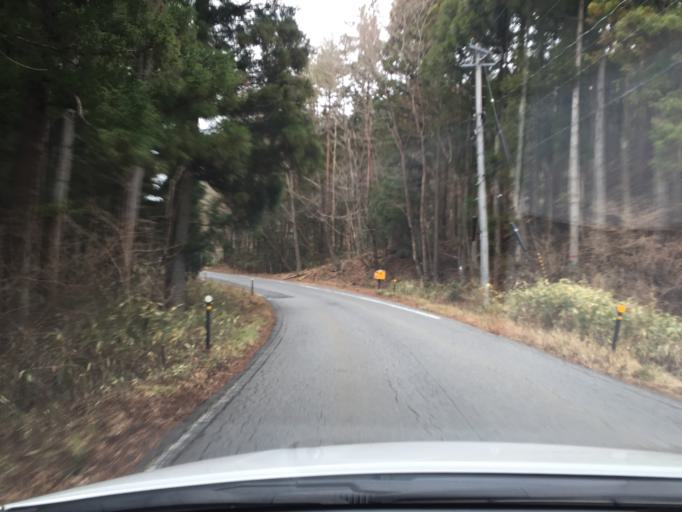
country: JP
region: Fukushima
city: Iwaki
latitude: 37.1169
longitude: 140.7794
